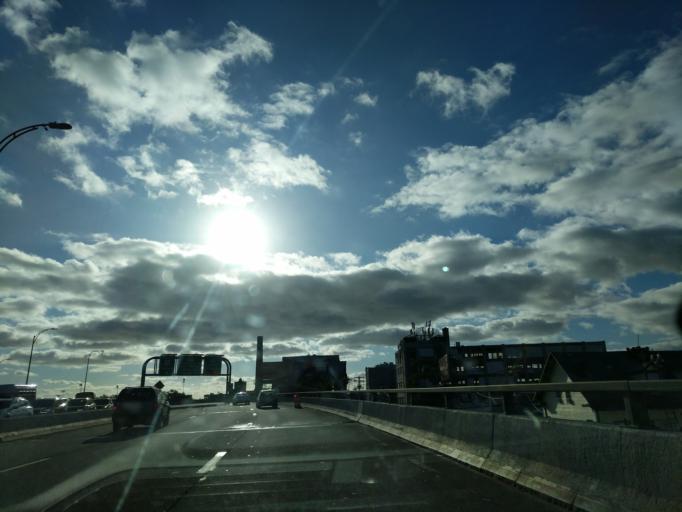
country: US
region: Massachusetts
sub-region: Suffolk County
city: Chelsea
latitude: 42.3729
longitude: -71.0352
